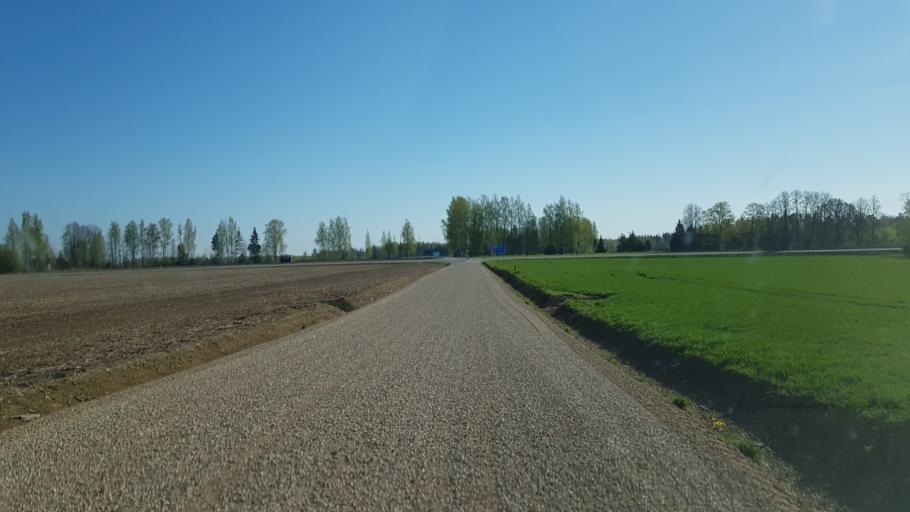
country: EE
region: Polvamaa
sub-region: Raepina vald
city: Rapina
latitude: 58.1318
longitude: 27.2653
